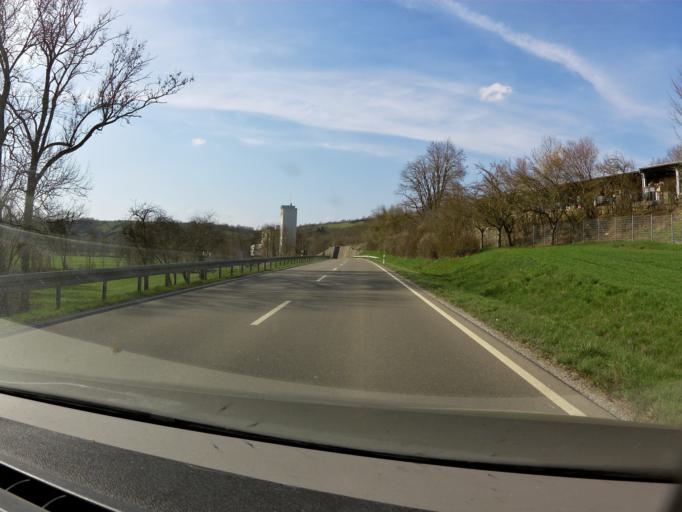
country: DE
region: Bavaria
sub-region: Regierungsbezirk Unterfranken
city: Bieberehren
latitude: 49.5194
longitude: 10.0056
